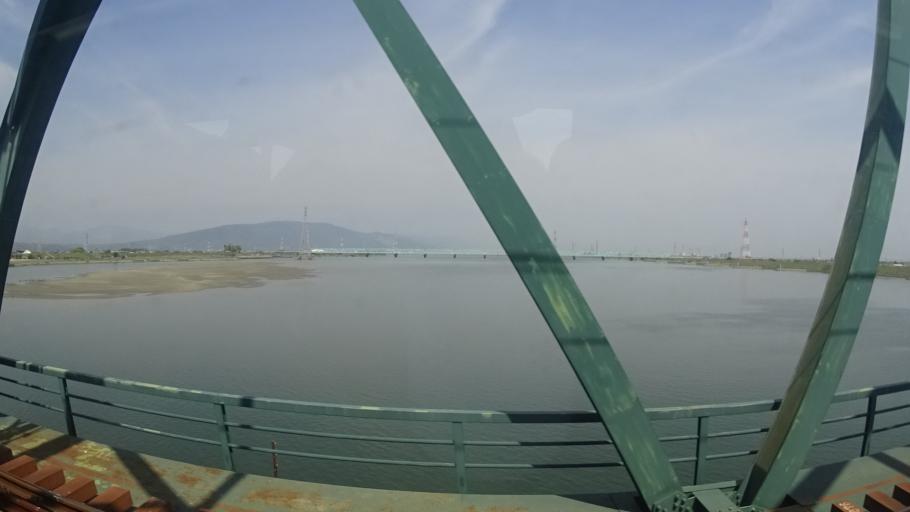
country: JP
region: Aichi
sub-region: Tsushima-shi
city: Tsushima
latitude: 35.1061
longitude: 136.7111
